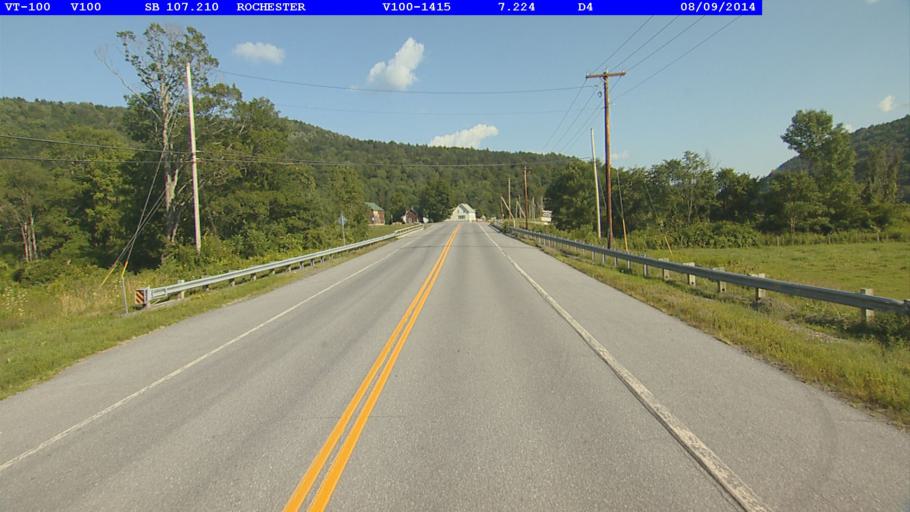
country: US
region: Vermont
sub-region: Orange County
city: Randolph
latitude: 43.8983
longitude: -72.8222
